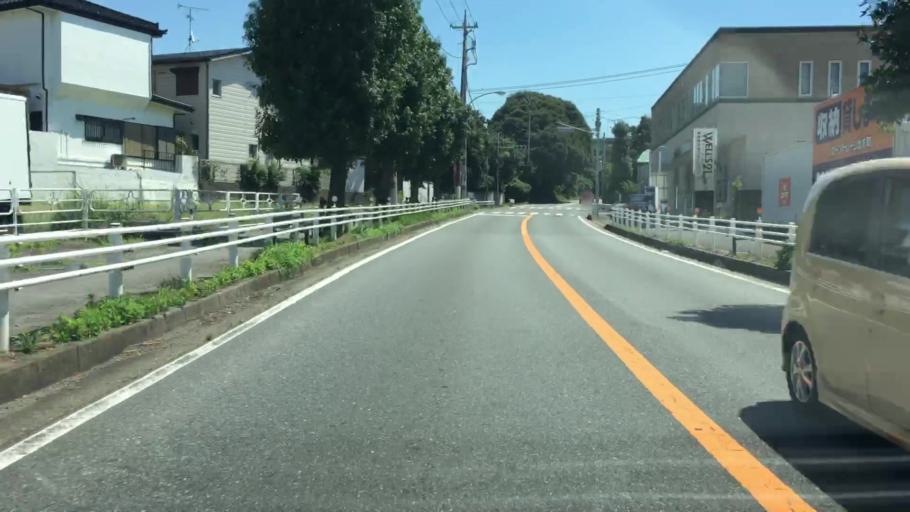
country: JP
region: Chiba
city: Funabashi
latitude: 35.7348
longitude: 139.9580
